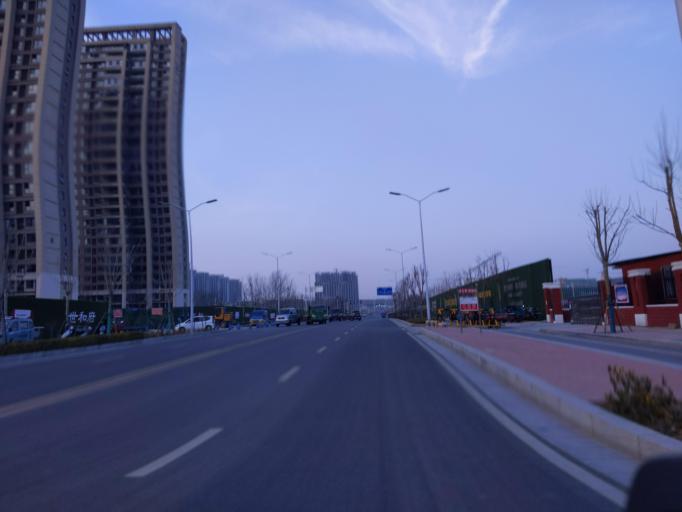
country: CN
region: Henan Sheng
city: Puyang
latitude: 35.8080
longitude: 115.0113
